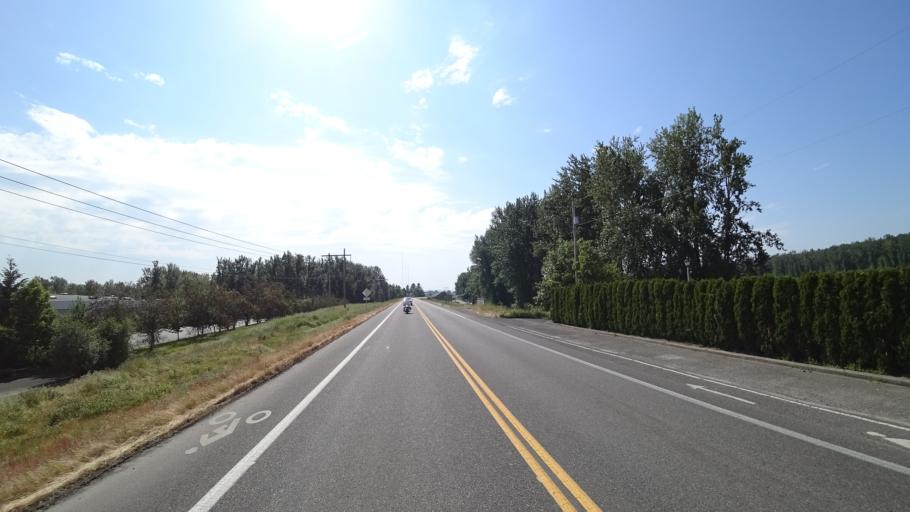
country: US
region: Oregon
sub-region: Multnomah County
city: Fairview
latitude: 45.5587
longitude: -122.4749
